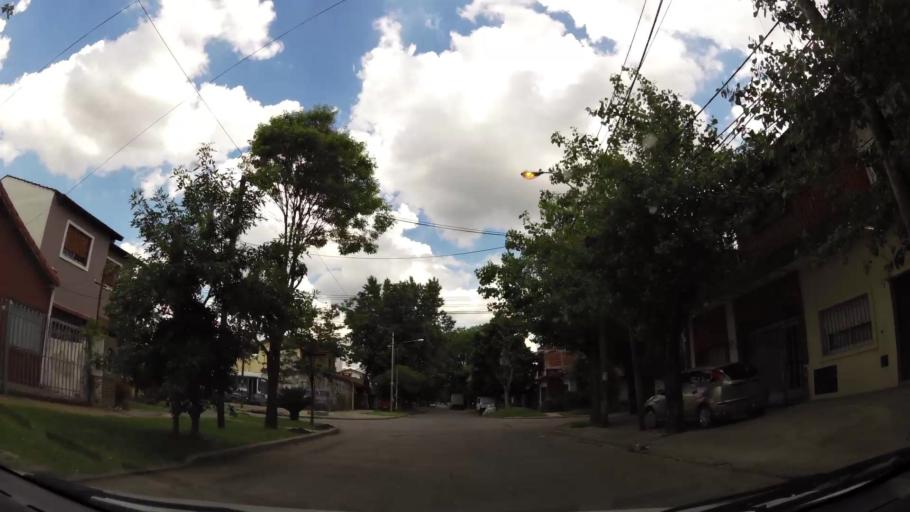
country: AR
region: Buenos Aires
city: Ituzaingo
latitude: -34.6505
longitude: -58.6683
